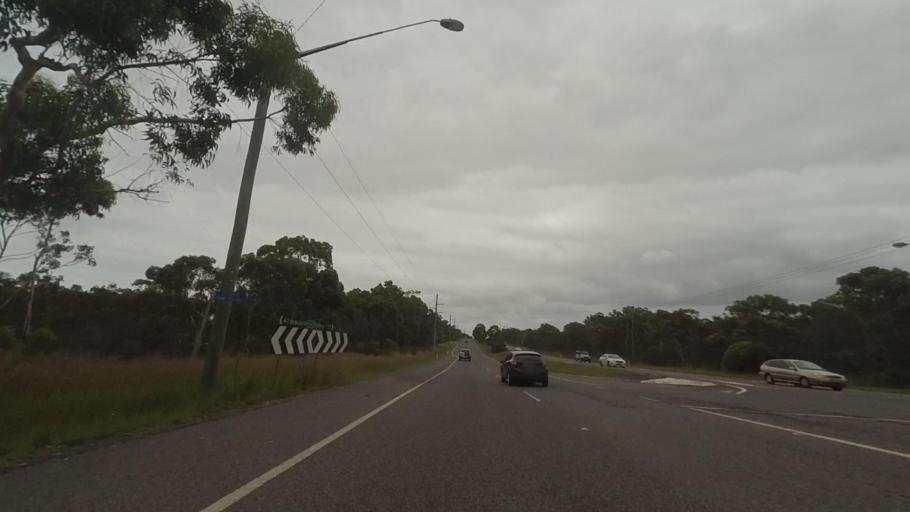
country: AU
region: New South Wales
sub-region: Wyong Shire
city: Kingfisher Shores
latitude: -33.1866
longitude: 151.5843
